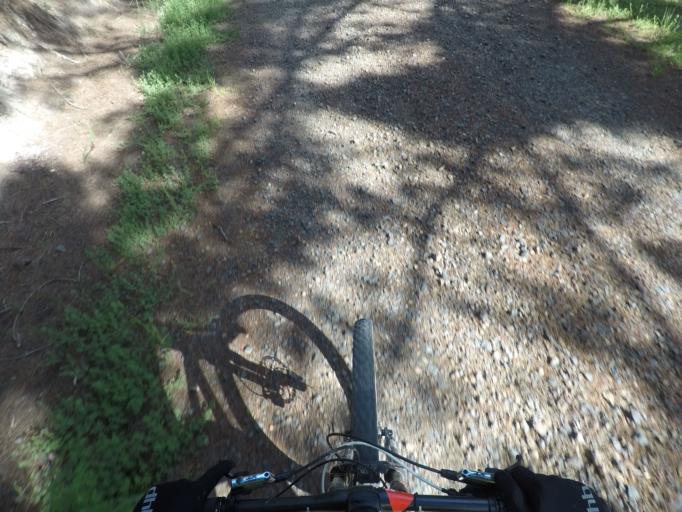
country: NZ
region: Auckland
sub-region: Auckland
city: Muriwai Beach
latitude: -36.7416
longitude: 174.5748
